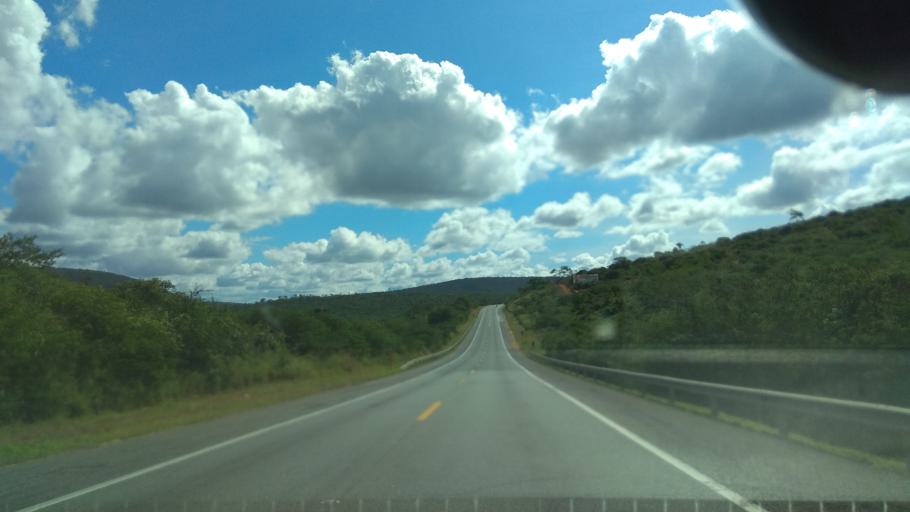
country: BR
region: Bahia
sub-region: Santa Ines
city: Santa Ines
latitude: -13.3122
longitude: -40.0203
